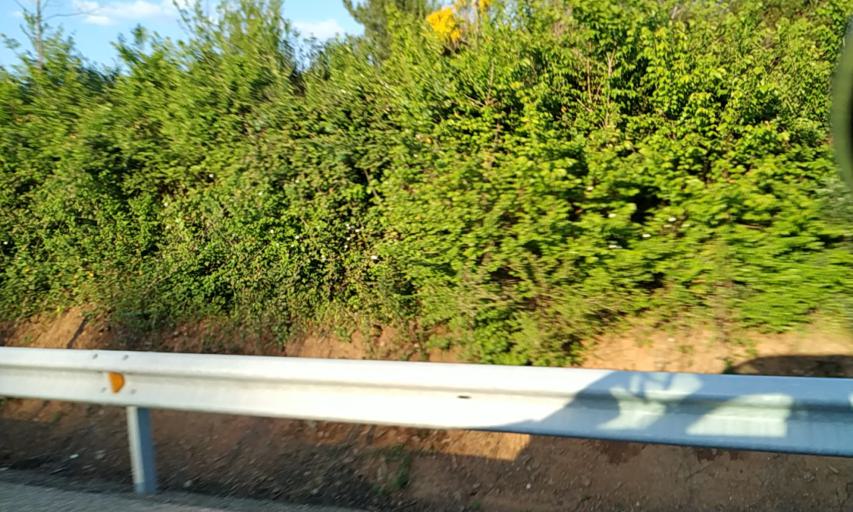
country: PT
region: Portalegre
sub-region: Portalegre
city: Sao Juliao
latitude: 39.3467
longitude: -7.2757
